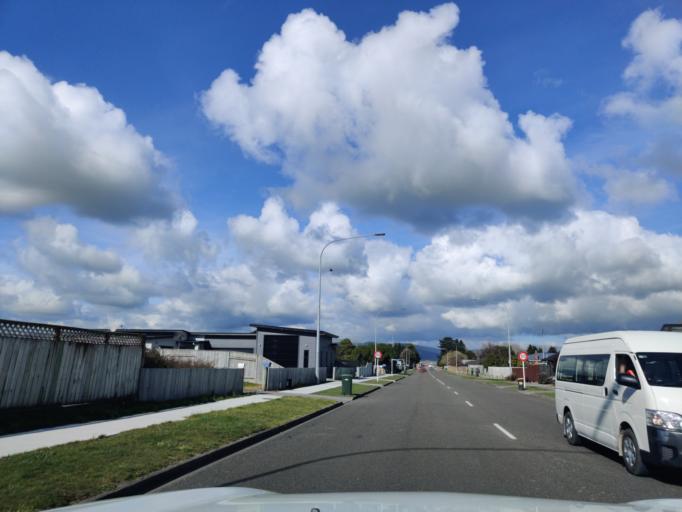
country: NZ
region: Manawatu-Wanganui
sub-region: Palmerston North City
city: Palmerston North
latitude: -40.3252
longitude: 175.6618
